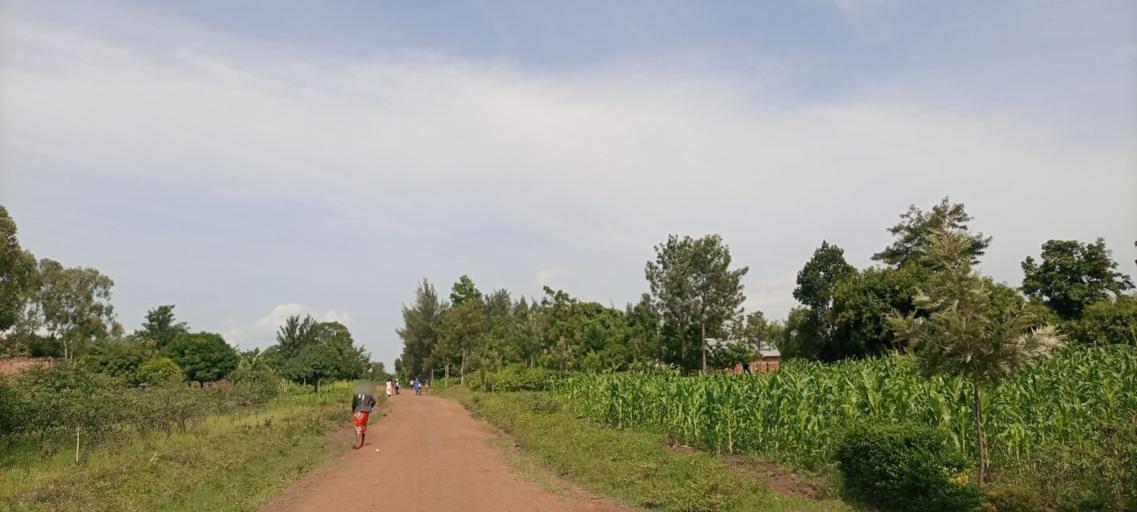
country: UG
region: Eastern Region
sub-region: Mbale District
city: Mbale
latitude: 1.1349
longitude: 34.0555
